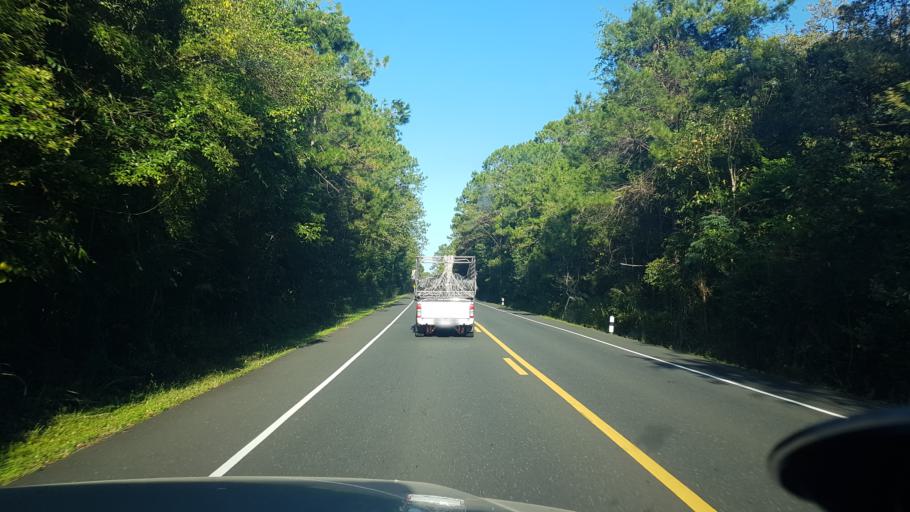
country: TH
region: Phetchabun
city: Nam Nao
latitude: 16.7069
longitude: 101.6043
